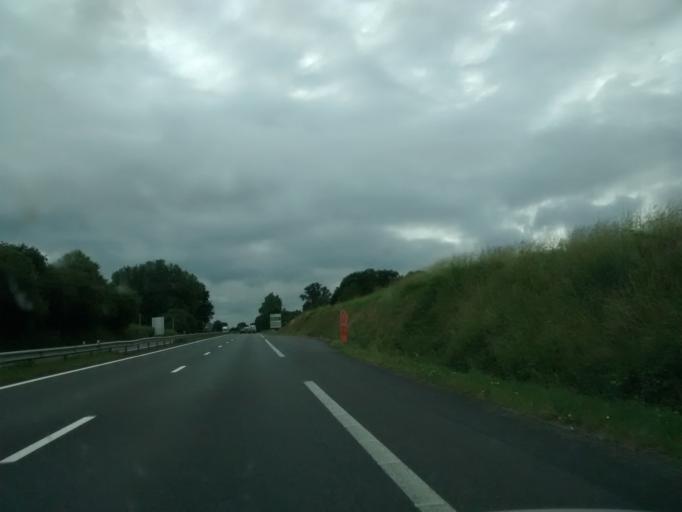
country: FR
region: Brittany
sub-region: Departement des Cotes-d'Armor
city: Graces
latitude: 48.5599
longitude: -3.1836
